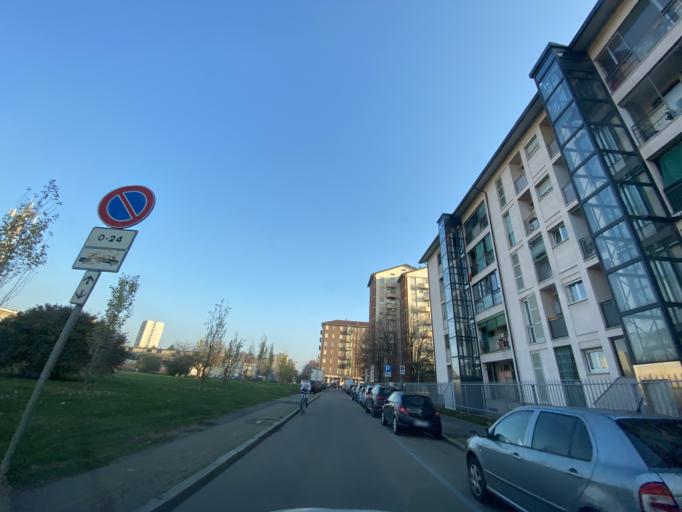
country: IT
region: Lombardy
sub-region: Citta metropolitana di Milano
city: Bresso
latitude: 45.5119
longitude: 9.1994
